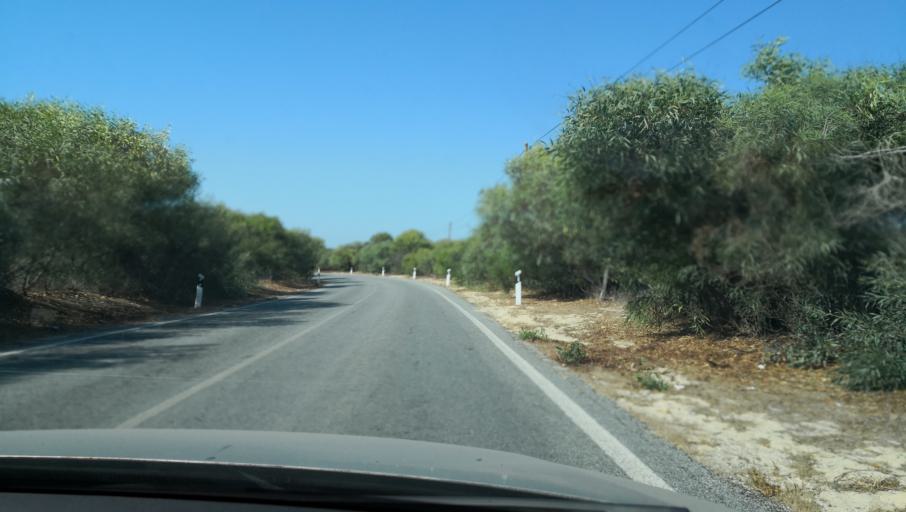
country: PT
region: Setubal
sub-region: Setubal
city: Setubal
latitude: 38.3887
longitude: -8.8002
